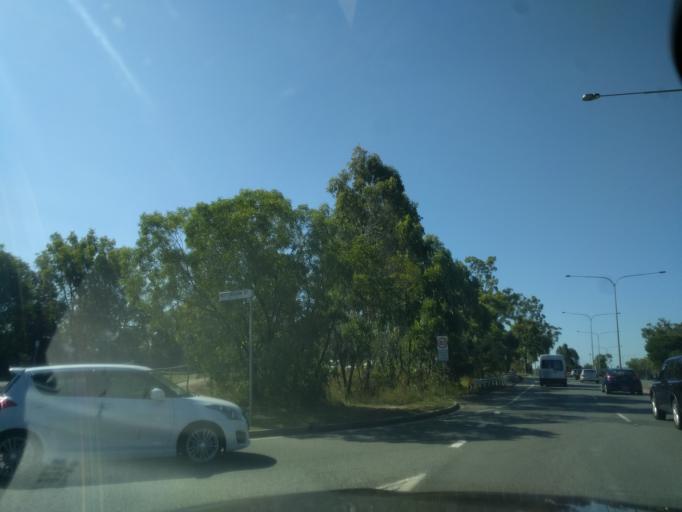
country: AU
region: Queensland
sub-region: Brisbane
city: Sunnybank Hills
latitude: -27.6302
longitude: 153.0465
